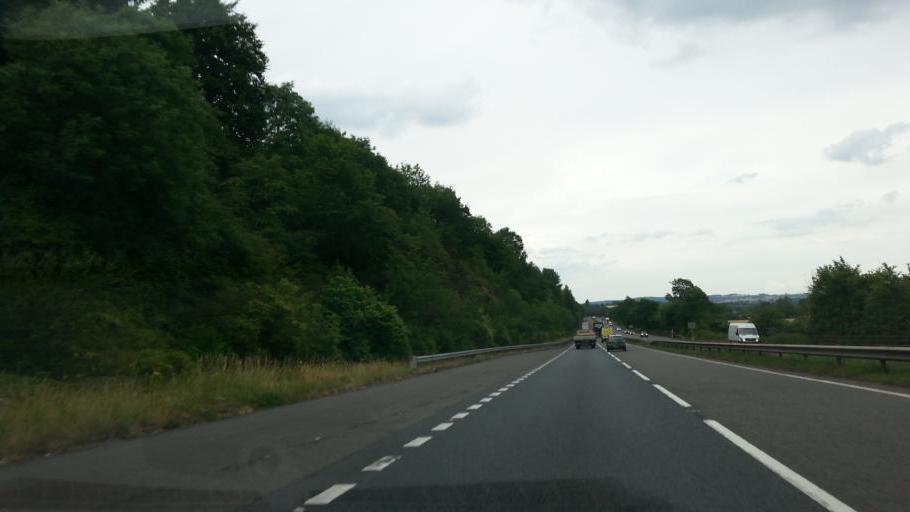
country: GB
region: England
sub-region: Herefordshire
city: Marstow
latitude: 51.8961
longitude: -2.6326
